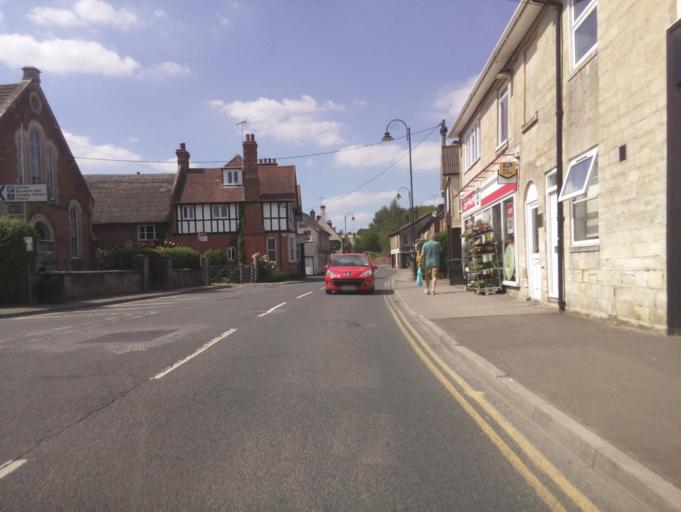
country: GB
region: England
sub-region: Wiltshire
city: Pewsey
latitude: 51.3399
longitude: -1.7659
